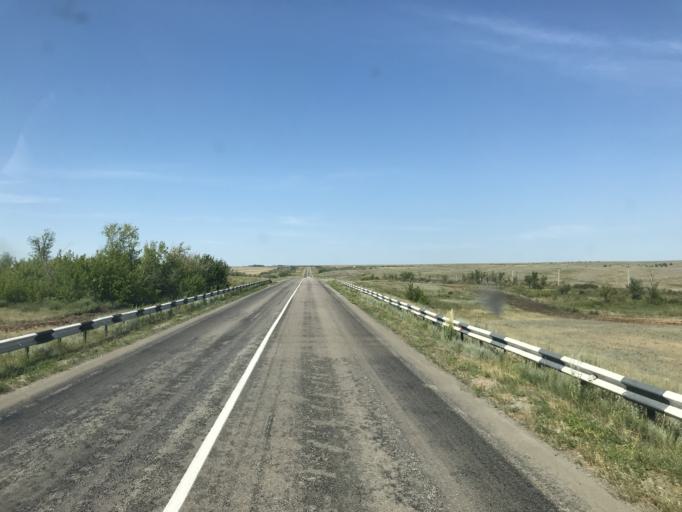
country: KZ
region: Aqtoebe
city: Martuk
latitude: 50.2342
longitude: 56.6625
